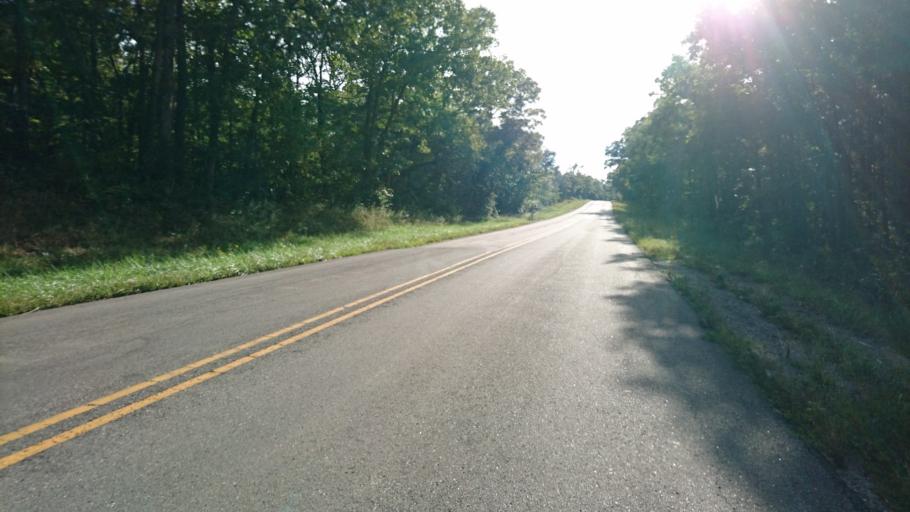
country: US
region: Missouri
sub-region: Crawford County
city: Cuba
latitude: 38.0992
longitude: -91.3535
